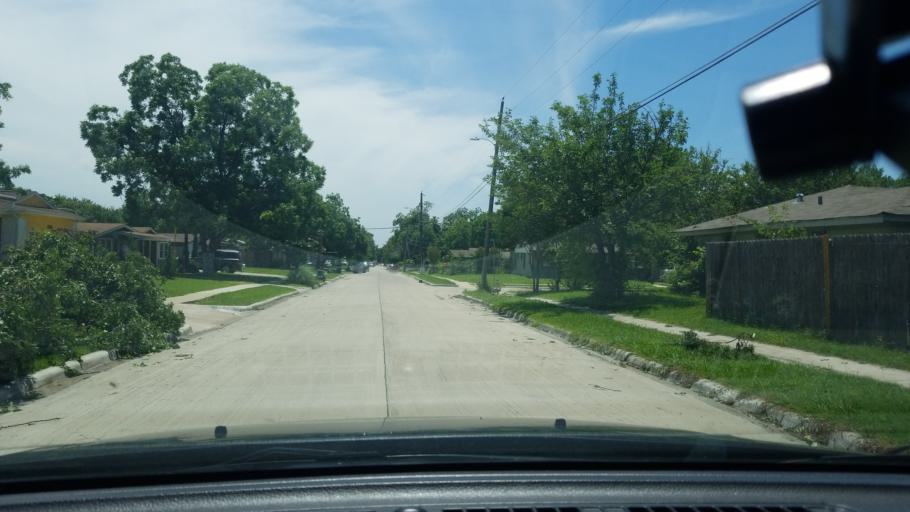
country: US
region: Texas
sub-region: Dallas County
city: Mesquite
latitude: 32.7883
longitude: -96.6167
